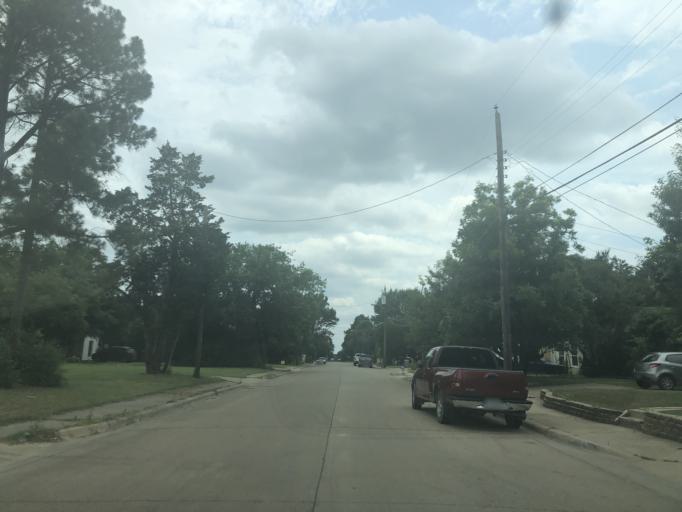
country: US
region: Texas
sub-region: Dallas County
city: Irving
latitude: 32.8076
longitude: -96.9300
